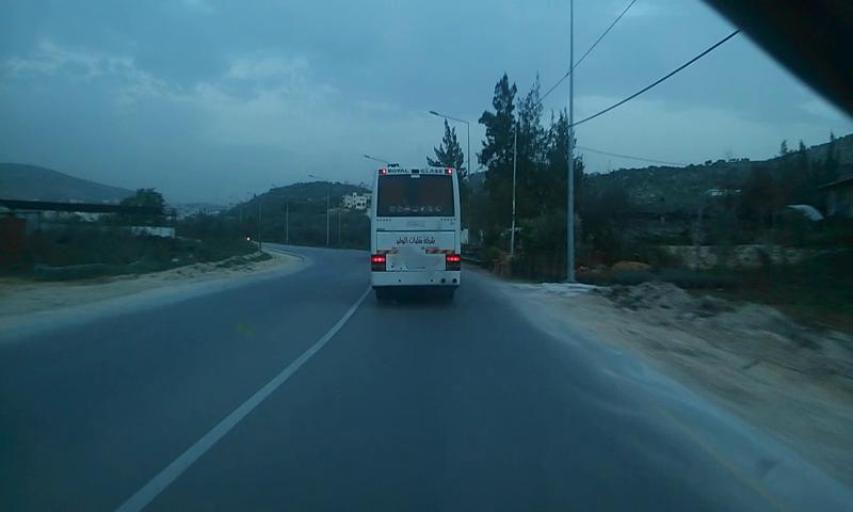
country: PS
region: West Bank
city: Kafr al Labad
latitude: 32.3118
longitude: 35.0971
